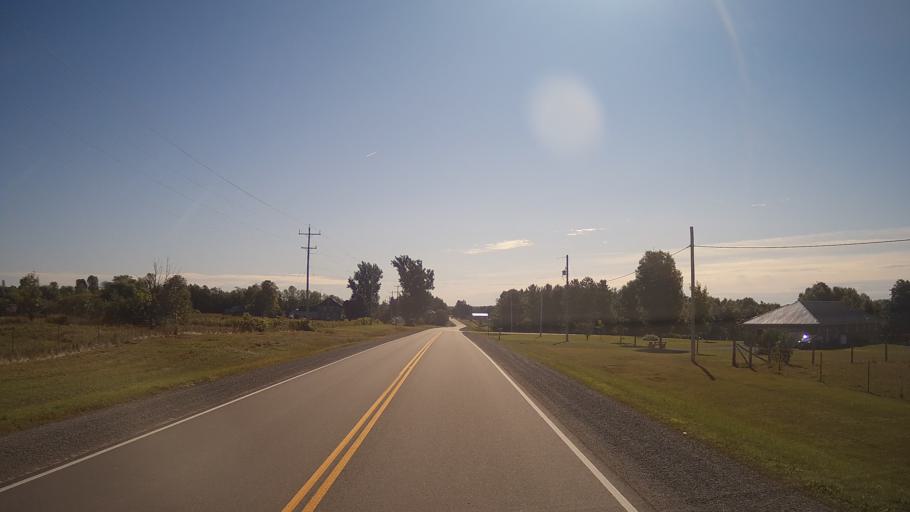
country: CA
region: Ontario
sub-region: Lanark County
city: Smiths Falls
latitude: 44.6244
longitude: -75.9725
